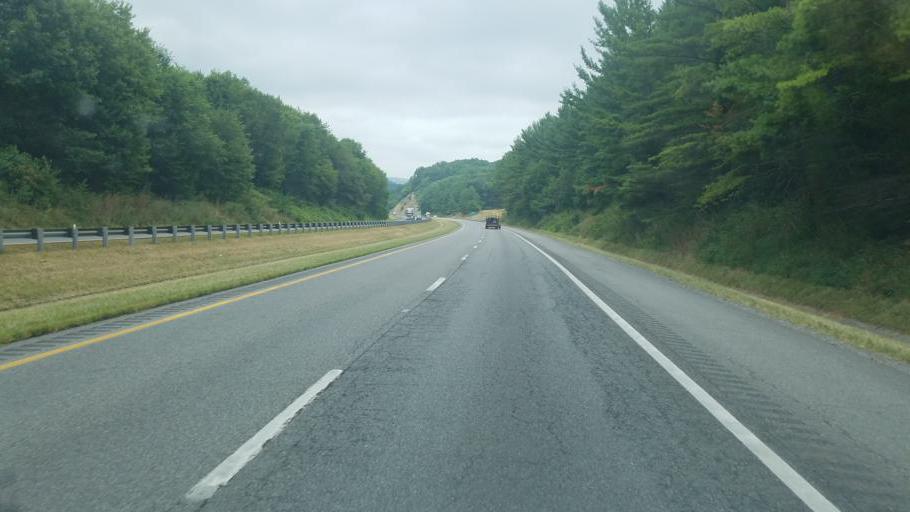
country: US
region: Virginia
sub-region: Bland County
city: Bland
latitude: 37.0629
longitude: -81.1285
